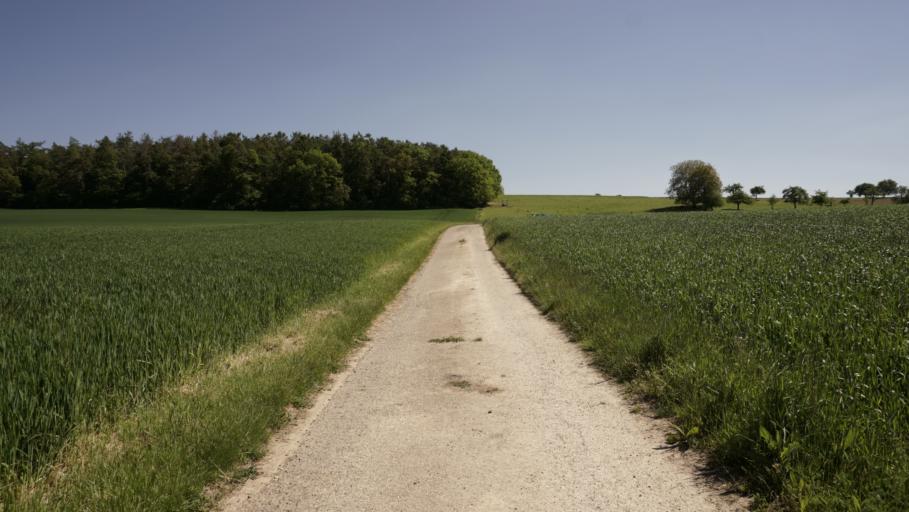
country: DE
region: Baden-Wuerttemberg
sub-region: Karlsruhe Region
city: Mosbach
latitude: 49.3713
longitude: 9.1828
